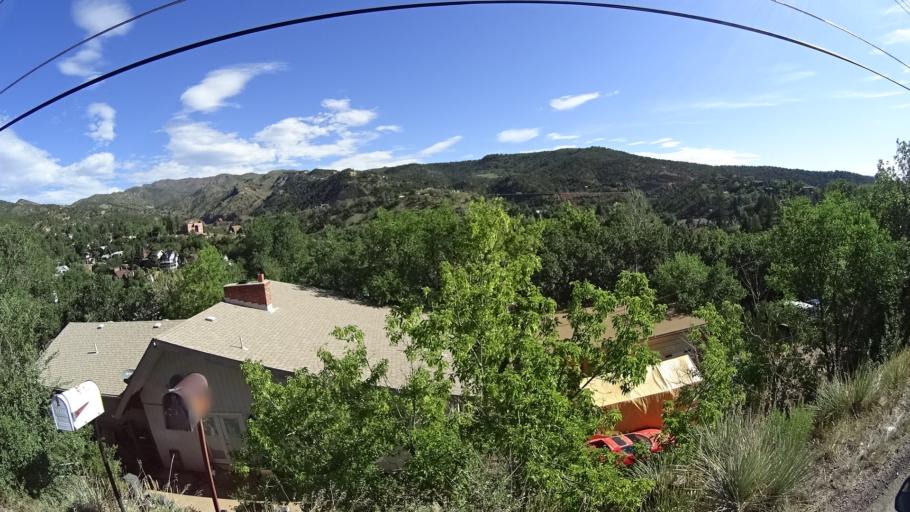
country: US
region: Colorado
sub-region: El Paso County
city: Manitou Springs
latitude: 38.8572
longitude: -104.9210
